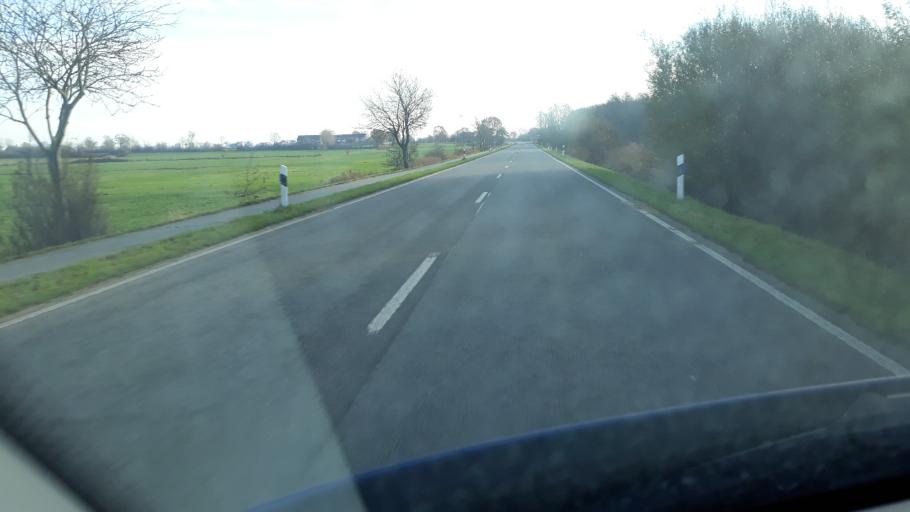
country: DE
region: Schleswig-Holstein
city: Maasholm
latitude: 54.6605
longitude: 9.9985
